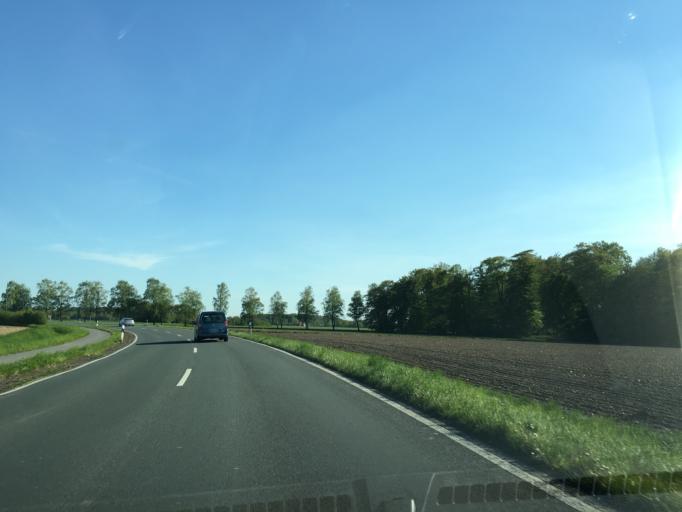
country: DE
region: North Rhine-Westphalia
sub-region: Regierungsbezirk Munster
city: Senden
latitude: 51.8361
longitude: 7.5174
